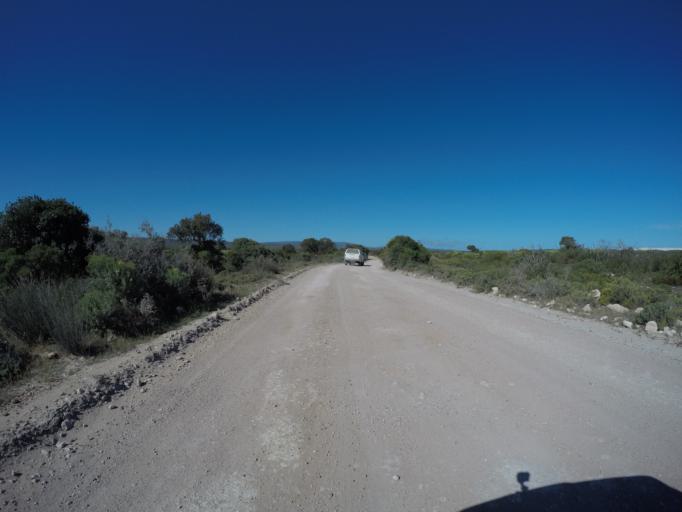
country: ZA
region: Western Cape
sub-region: Overberg District Municipality
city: Bredasdorp
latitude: -34.4560
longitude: 20.4167
